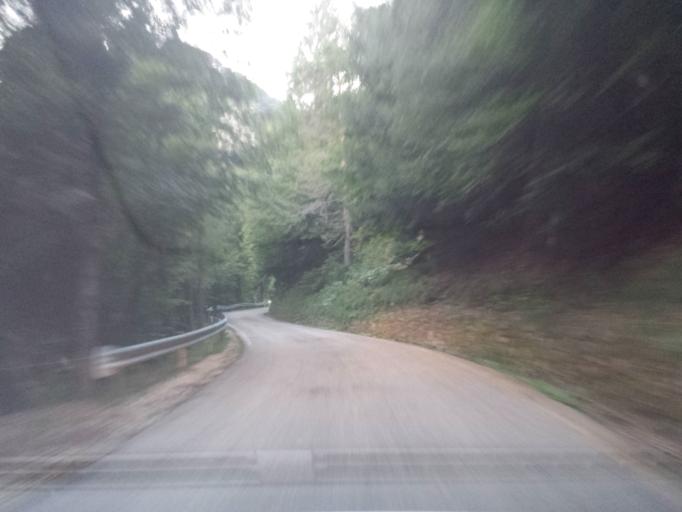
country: IT
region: Veneto
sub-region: Provincia di Vicenza
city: Recoaro Terme
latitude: 45.7226
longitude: 11.1770
